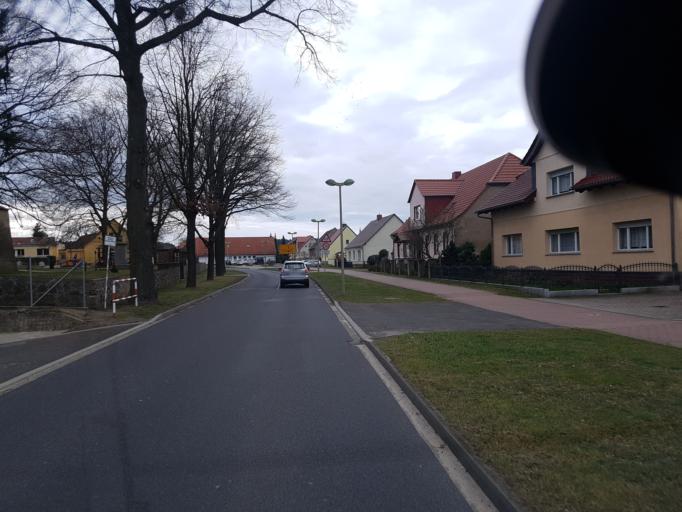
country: DE
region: Brandenburg
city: Gross Lindow
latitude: 52.1437
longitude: 14.5313
